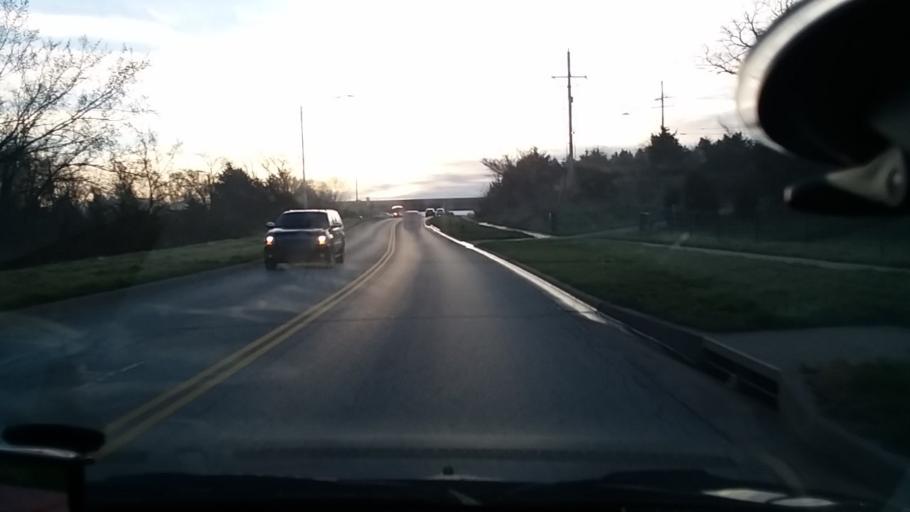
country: US
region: Kansas
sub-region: Johnson County
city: Olathe
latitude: 38.9126
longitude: -94.8562
